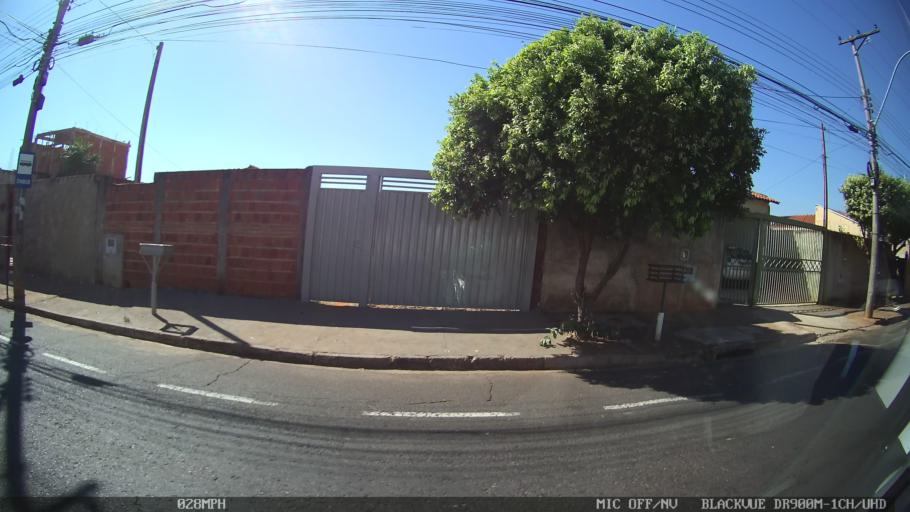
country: BR
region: Sao Paulo
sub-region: Sao Jose Do Rio Preto
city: Sao Jose do Rio Preto
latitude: -20.7631
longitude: -49.4011
